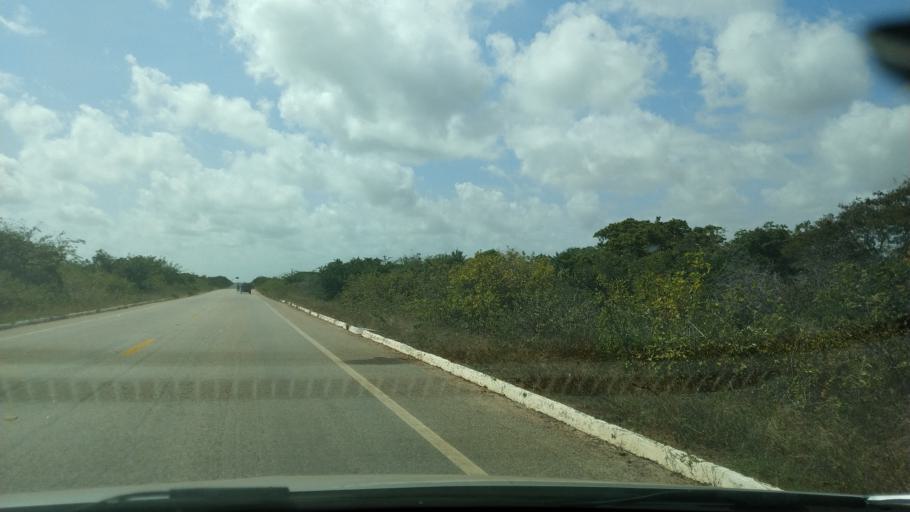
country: BR
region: Rio Grande do Norte
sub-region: Touros
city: Touros
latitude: -5.1922
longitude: -35.5067
